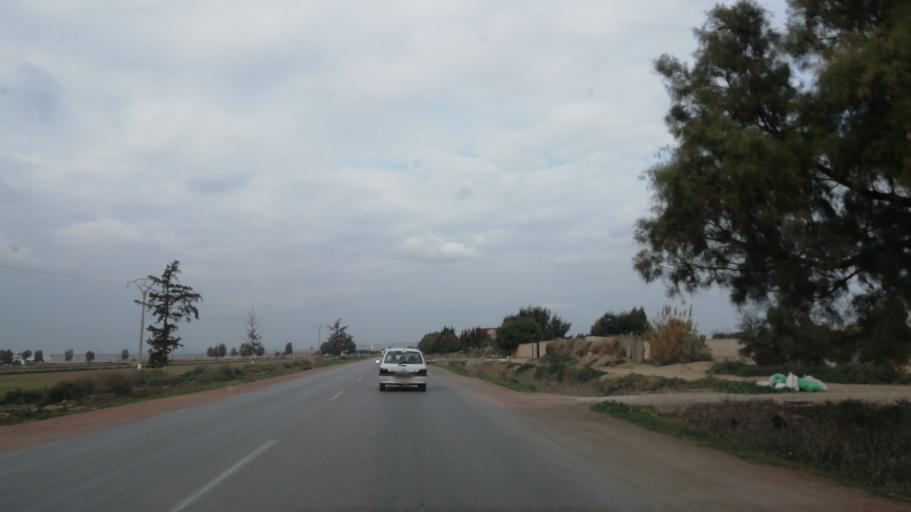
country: DZ
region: Mostaganem
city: Mostaganem
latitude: 35.6885
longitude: 0.0562
